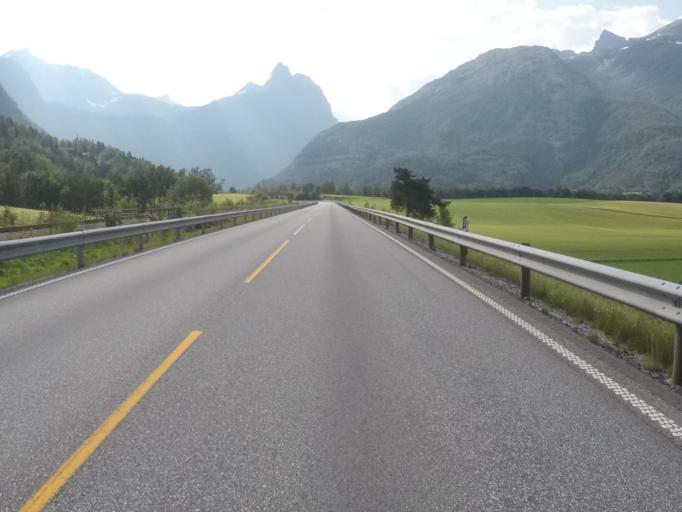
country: NO
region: More og Romsdal
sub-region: Rauma
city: Andalsnes
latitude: 62.5434
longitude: 7.7192
